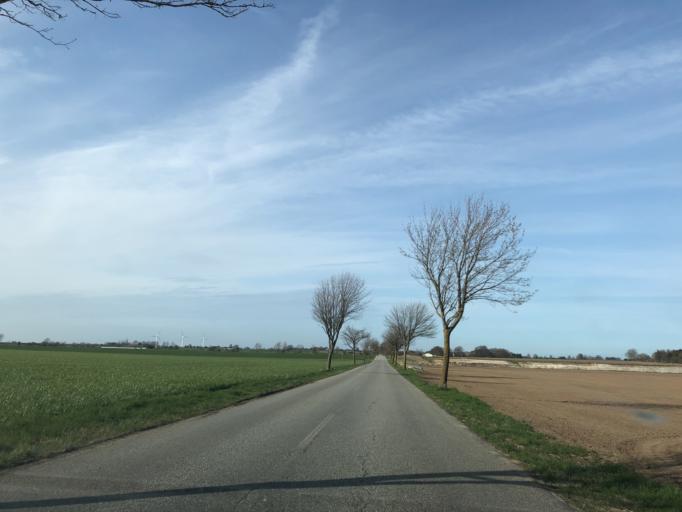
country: DK
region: Zealand
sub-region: Stevns Kommune
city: Store Heddinge
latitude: 55.3177
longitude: 12.4351
